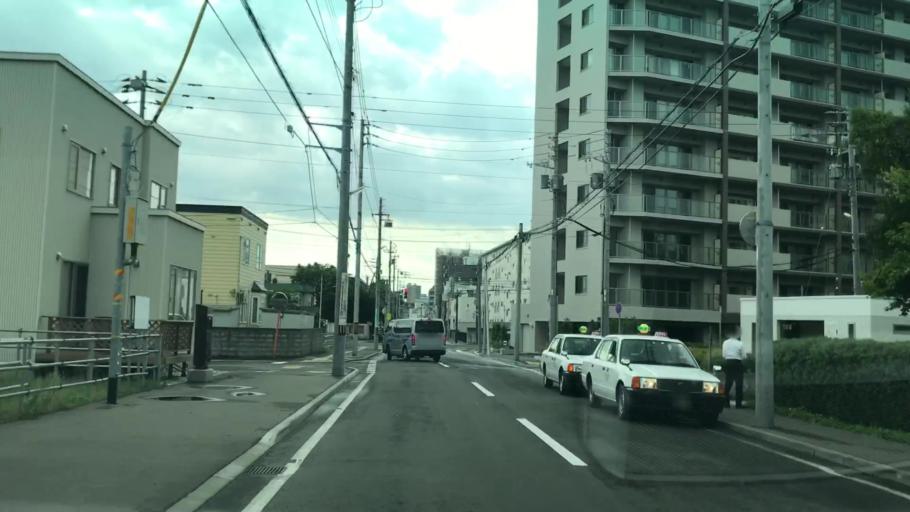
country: JP
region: Hokkaido
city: Sapporo
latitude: 43.0738
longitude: 141.3112
